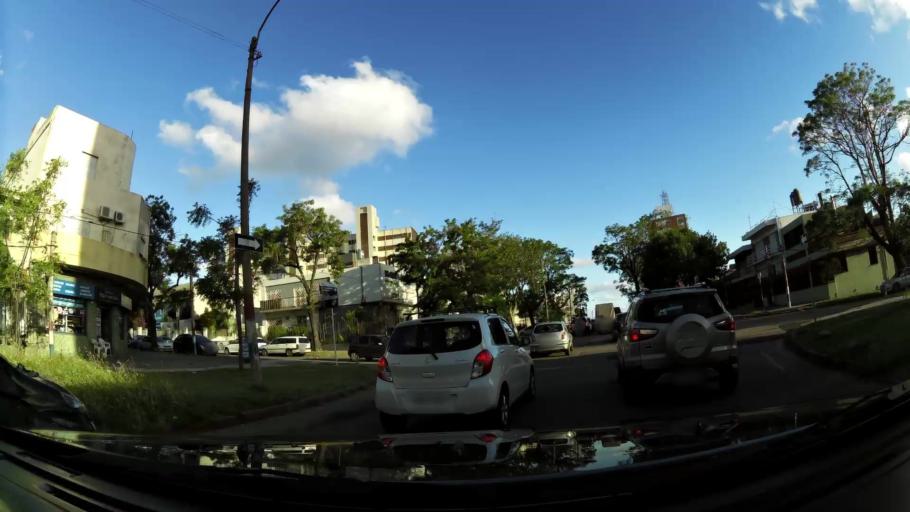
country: UY
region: Montevideo
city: Montevideo
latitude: -34.8871
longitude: -56.1489
